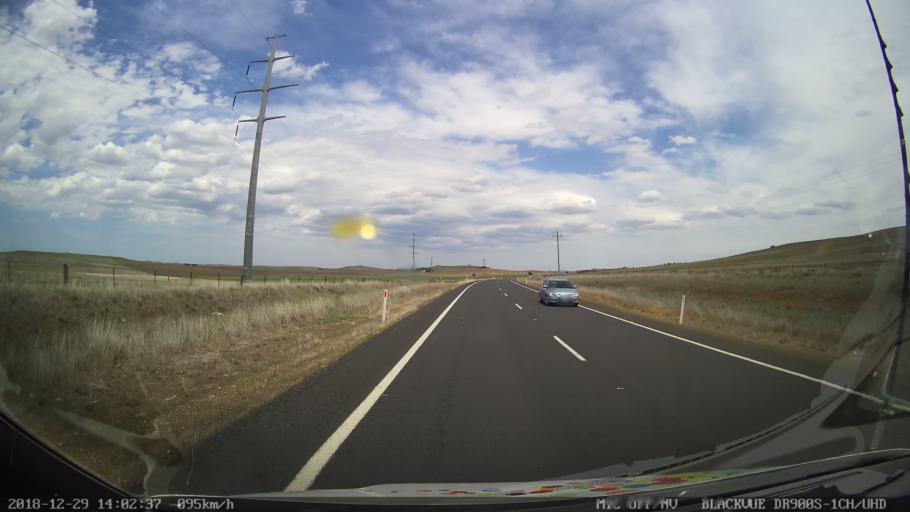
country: AU
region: New South Wales
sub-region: Cooma-Monaro
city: Cooma
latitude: -36.2901
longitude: 149.1788
